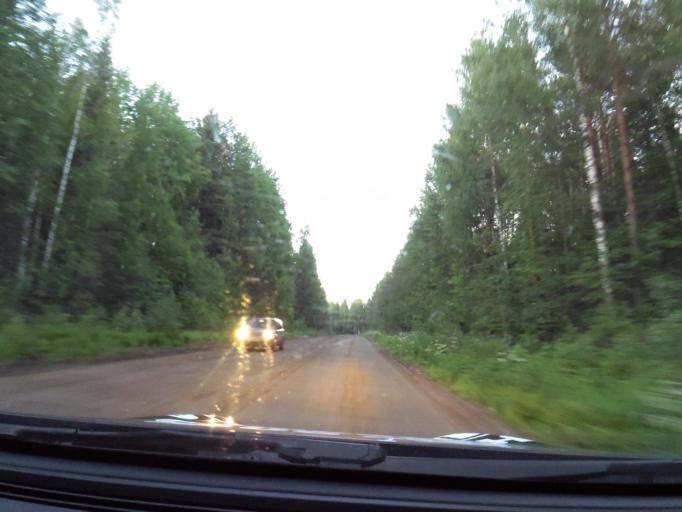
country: RU
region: Leningrad
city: Voznesen'ye
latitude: 60.8545
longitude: 35.9063
